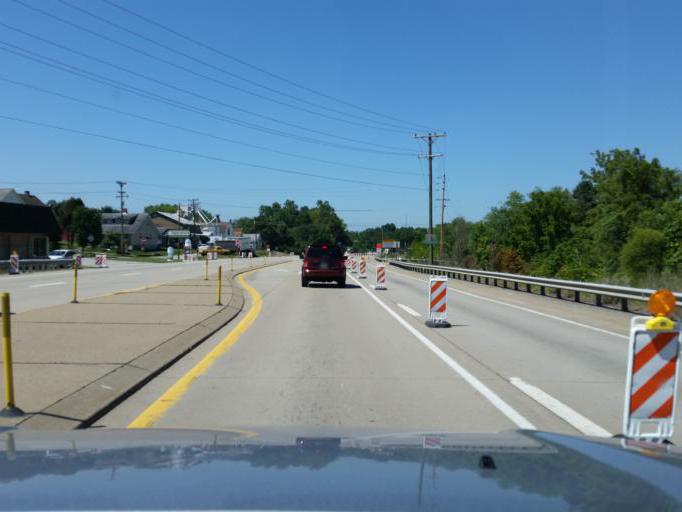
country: US
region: Pennsylvania
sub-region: Westmoreland County
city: Latrobe
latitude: 40.3977
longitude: -79.4252
